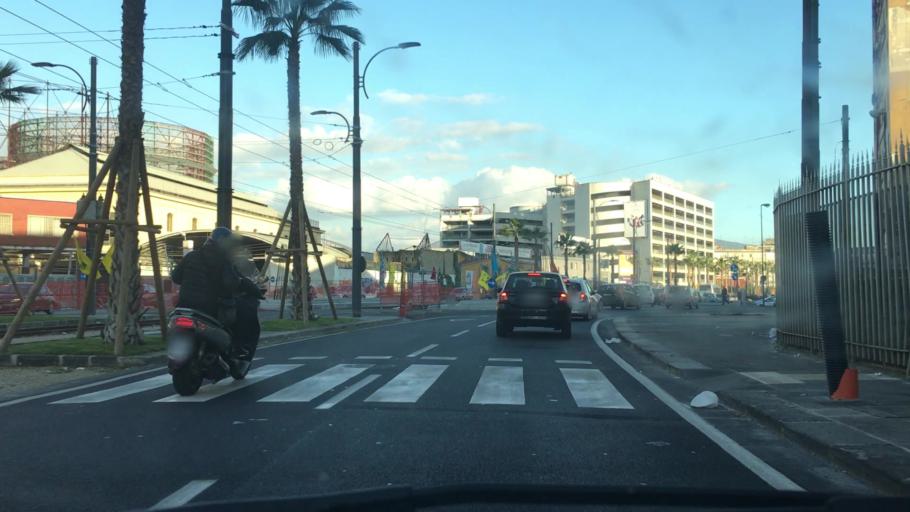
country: IT
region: Campania
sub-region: Provincia di Napoli
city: Napoli
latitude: 40.8467
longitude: 14.2769
